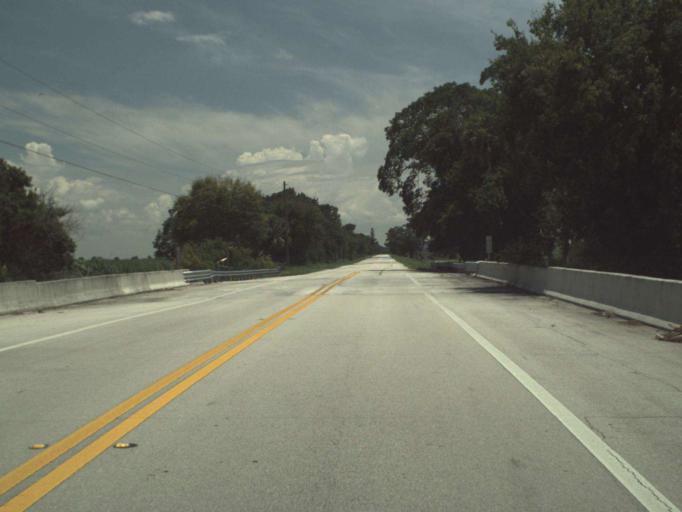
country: US
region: Florida
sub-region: Martin County
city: Indiantown
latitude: 27.0672
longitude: -80.6512
